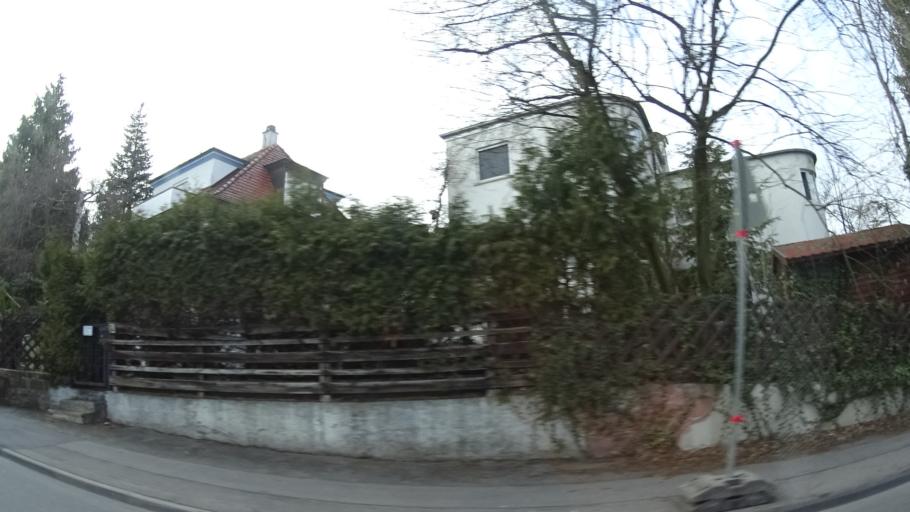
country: DE
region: Baden-Wuerttemberg
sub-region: Regierungsbezirk Stuttgart
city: Steinenbronn
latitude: 48.7230
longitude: 9.0934
